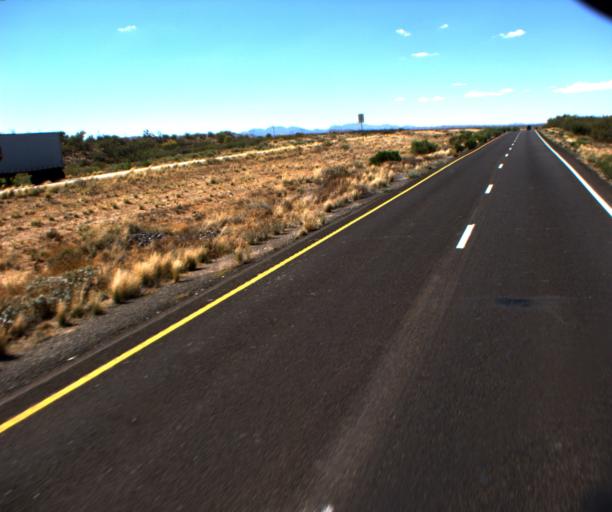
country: US
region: Arizona
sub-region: Yavapai County
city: Bagdad
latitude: 34.8329
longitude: -113.6312
